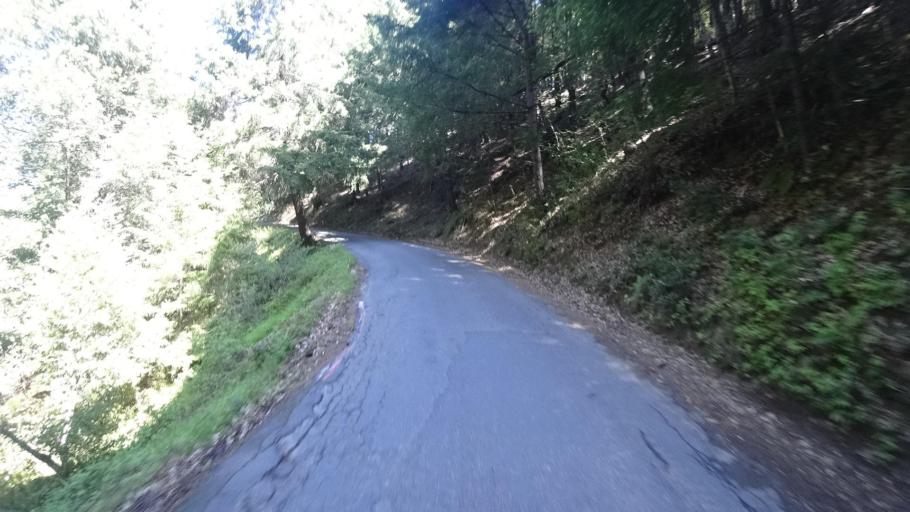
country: US
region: California
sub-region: Humboldt County
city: Redway
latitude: 40.1199
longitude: -123.9688
